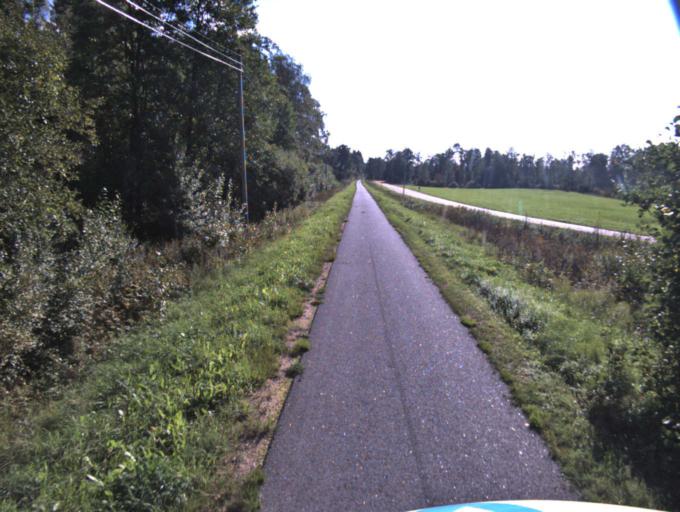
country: SE
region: Vaestra Goetaland
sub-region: Boras Kommun
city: Dalsjofors
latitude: 57.8225
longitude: 13.1560
